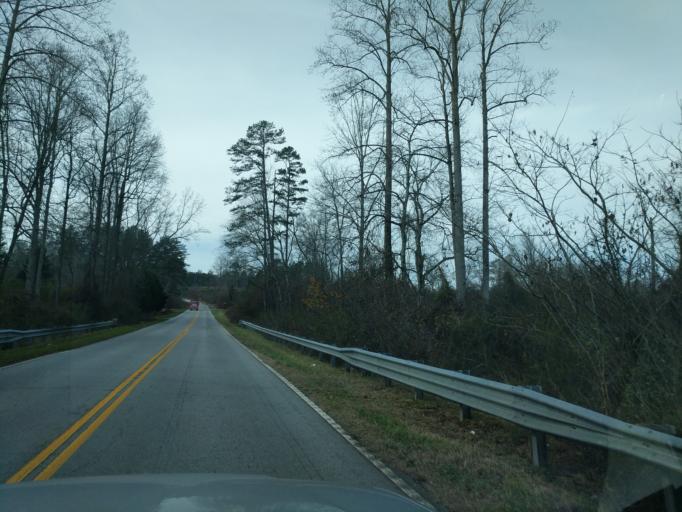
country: US
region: South Carolina
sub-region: Oconee County
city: Walhalla
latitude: 34.8026
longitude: -83.0228
